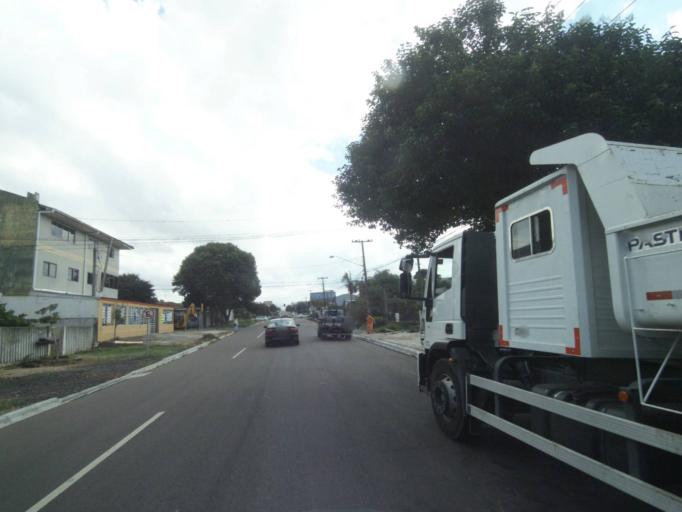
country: BR
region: Parana
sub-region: Pinhais
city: Pinhais
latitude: -25.4616
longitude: -49.2096
